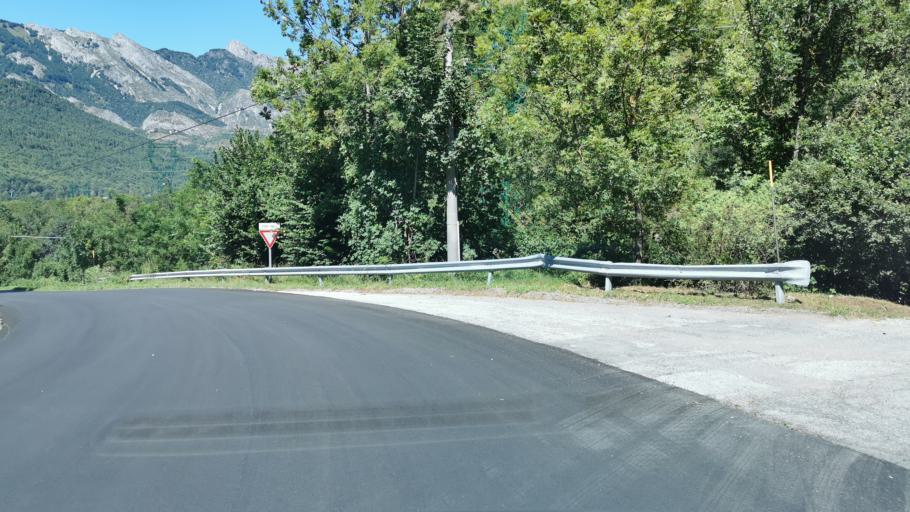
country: IT
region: Piedmont
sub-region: Provincia di Cuneo
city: Entracque
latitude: 44.2541
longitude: 7.3853
